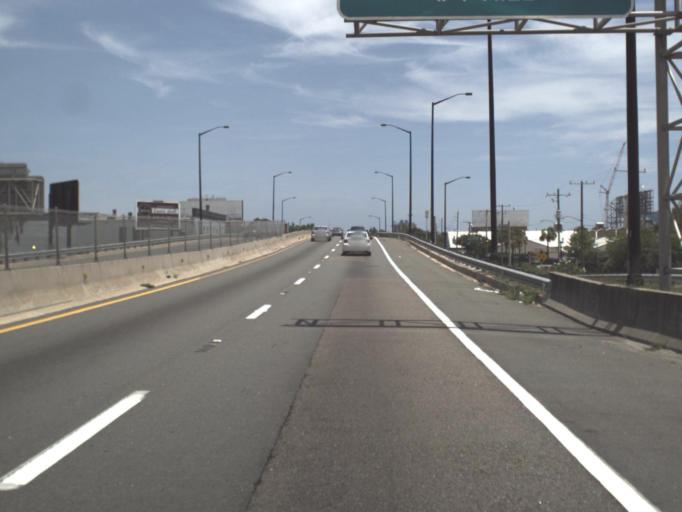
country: US
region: Florida
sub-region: Duval County
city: Jacksonville
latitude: 30.3287
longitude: -81.6445
